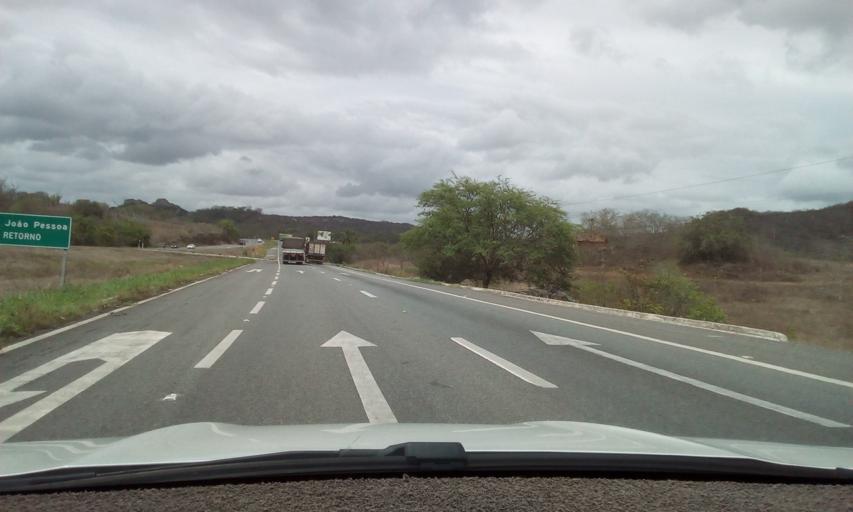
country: BR
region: Paraiba
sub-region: Massaranduba
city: Massaranduba
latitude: -7.2611
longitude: -35.7105
